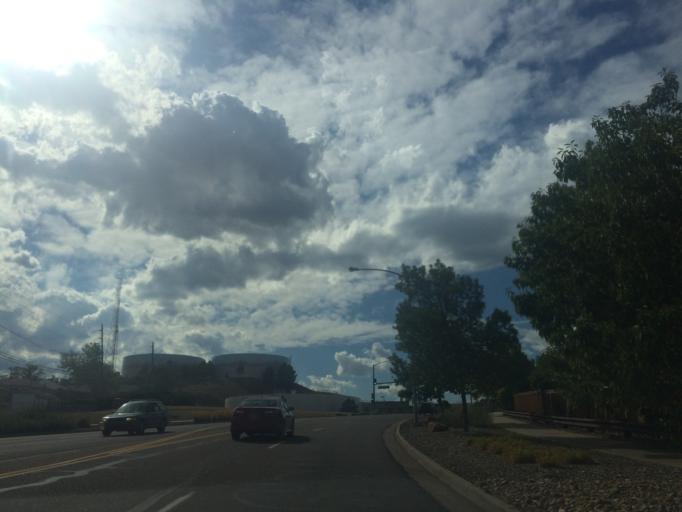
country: US
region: Colorado
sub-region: Adams County
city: Thornton
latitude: 39.8708
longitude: -104.9702
